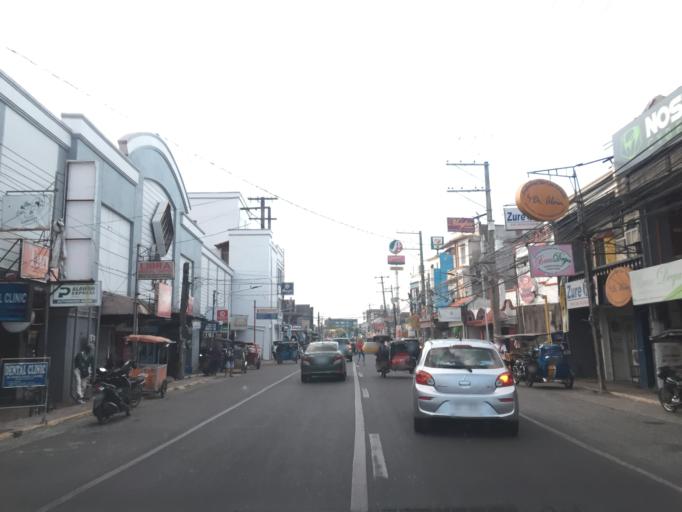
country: PH
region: Ilocos
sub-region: Province of Pangasinan
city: Bolingit
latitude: 15.9274
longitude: 120.3484
